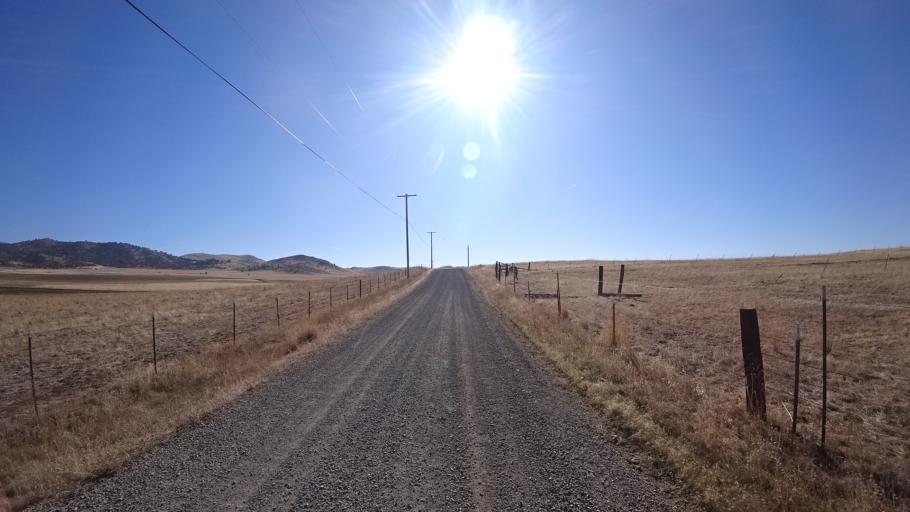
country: US
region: California
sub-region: Siskiyou County
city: Montague
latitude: 41.8016
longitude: -122.4159
